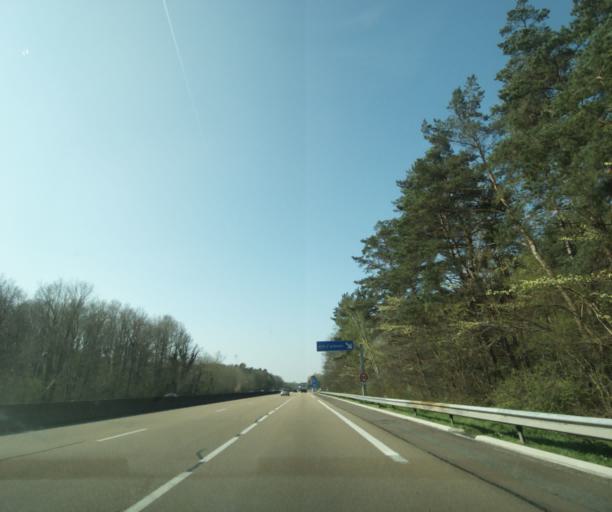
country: FR
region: Ile-de-France
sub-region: Departement de Seine-et-Marne
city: Arbonne-la-Foret
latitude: 48.4107
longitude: 2.5503
